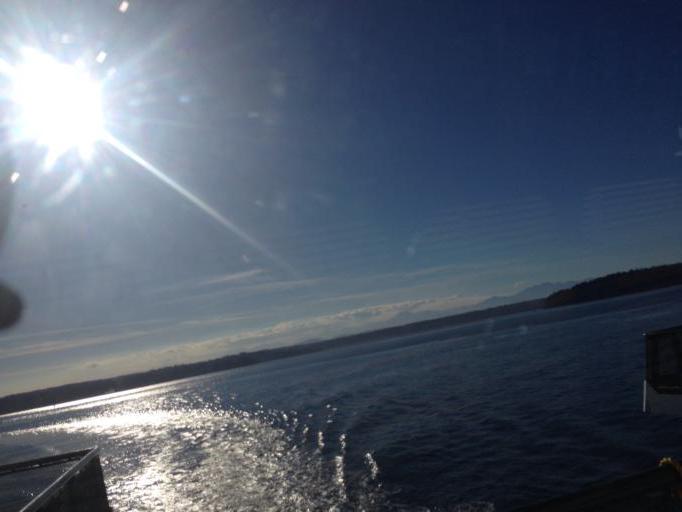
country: US
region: Washington
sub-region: Kitsap County
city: Southworth
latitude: 47.5165
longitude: -122.4556
